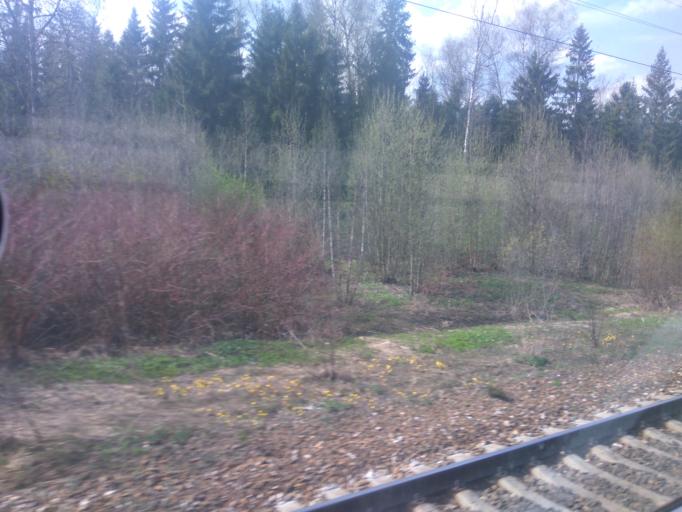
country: RU
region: Moskovskaya
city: Podosinki
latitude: 56.2152
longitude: 37.5269
